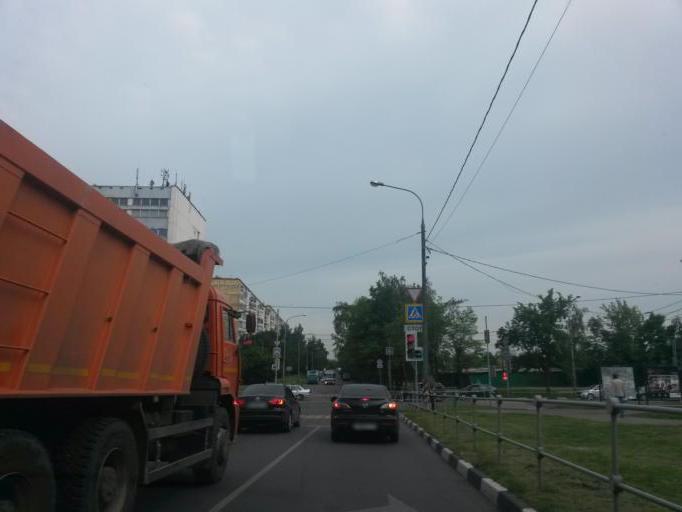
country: RU
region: Moscow
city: Orekhovo-Borisovo
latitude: 55.6044
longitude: 37.7346
